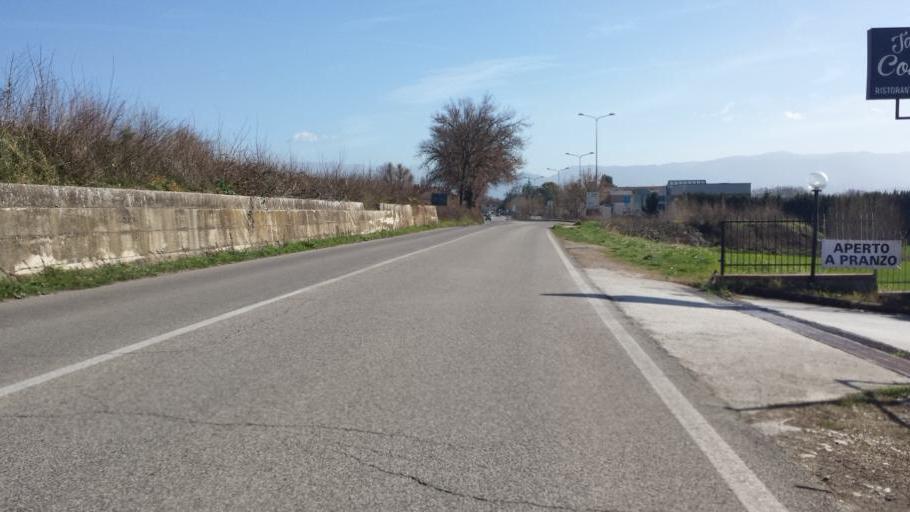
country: IT
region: Umbria
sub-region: Provincia di Terni
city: San Gemini
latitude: 42.5921
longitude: 12.5701
